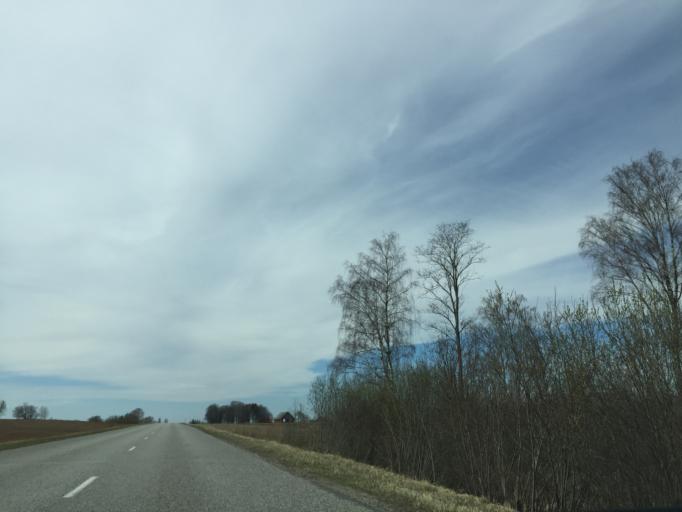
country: LV
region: Valkas Rajons
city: Valka
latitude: 57.7800
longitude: 25.9365
